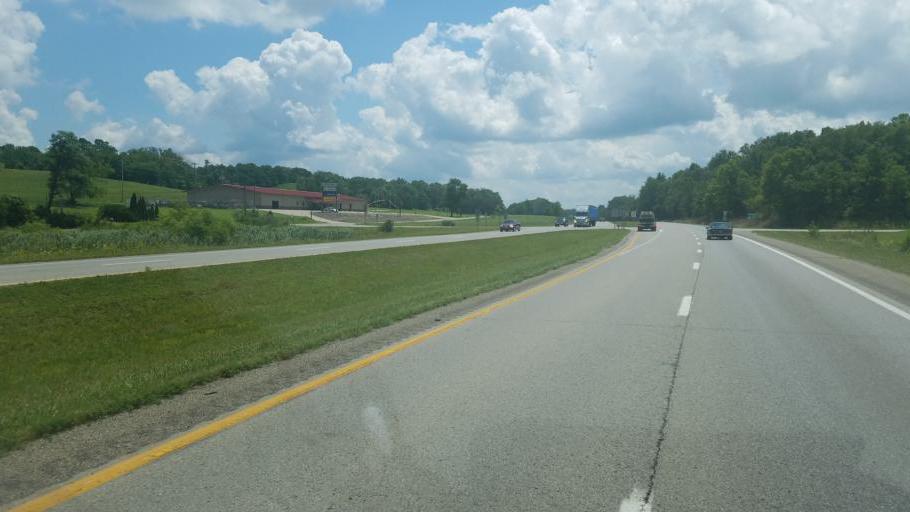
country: US
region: Ohio
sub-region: Jackson County
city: Jackson
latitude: 39.0152
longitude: -82.5749
